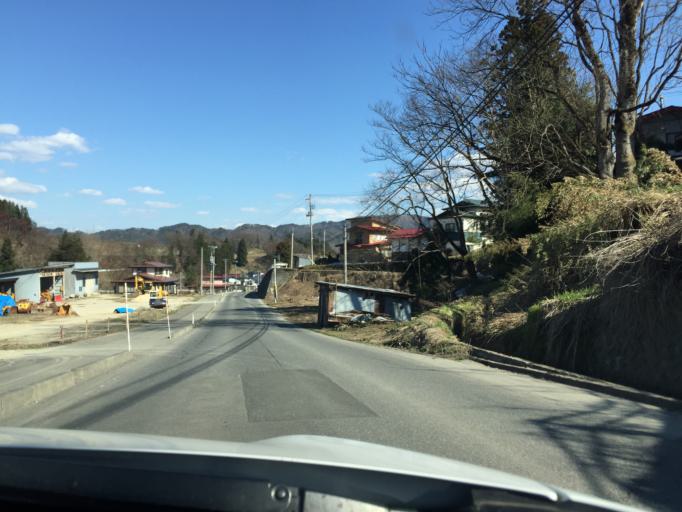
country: JP
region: Yamagata
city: Sagae
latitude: 38.2927
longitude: 140.1129
